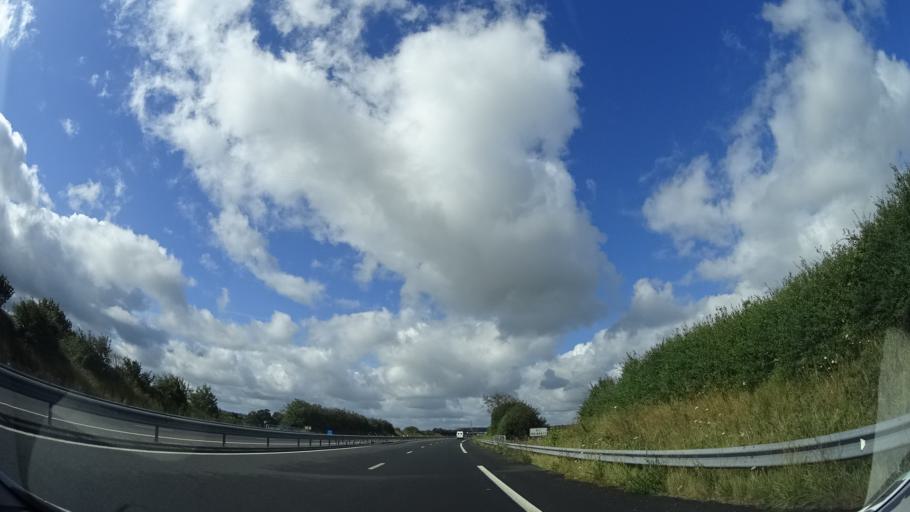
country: FR
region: Lower Normandy
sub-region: Departement de la Manche
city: Pont-Hebert
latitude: 49.1484
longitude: -1.1604
